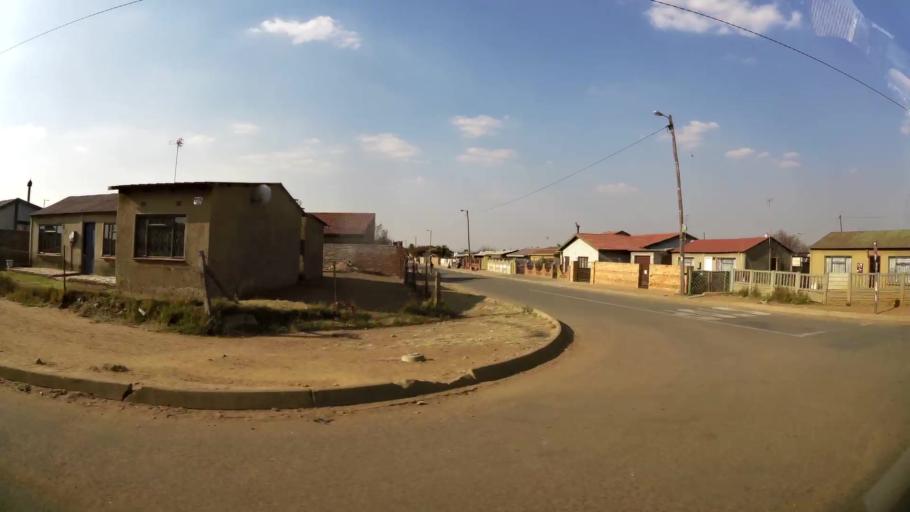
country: ZA
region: Gauteng
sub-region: Ekurhuleni Metropolitan Municipality
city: Brakpan
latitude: -26.1425
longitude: 28.4247
